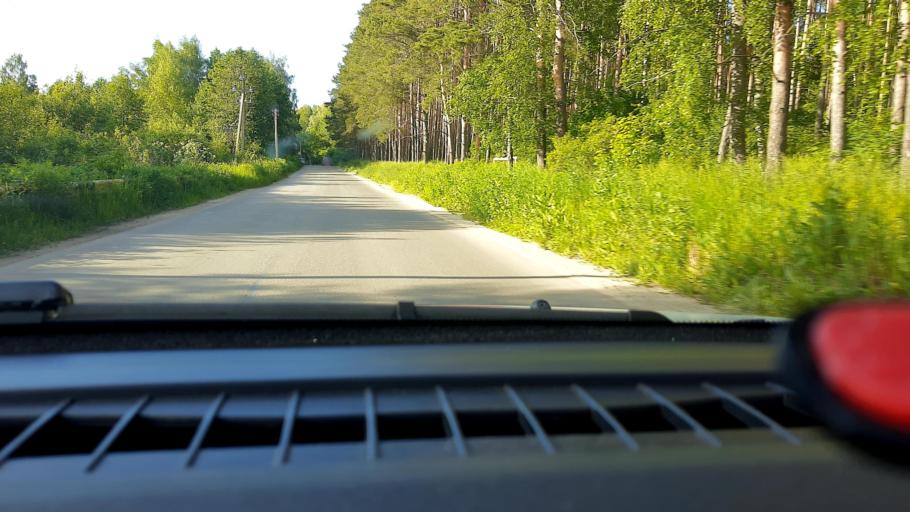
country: RU
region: Nizjnij Novgorod
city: Gorbatovka
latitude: 56.2286
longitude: 43.7628
